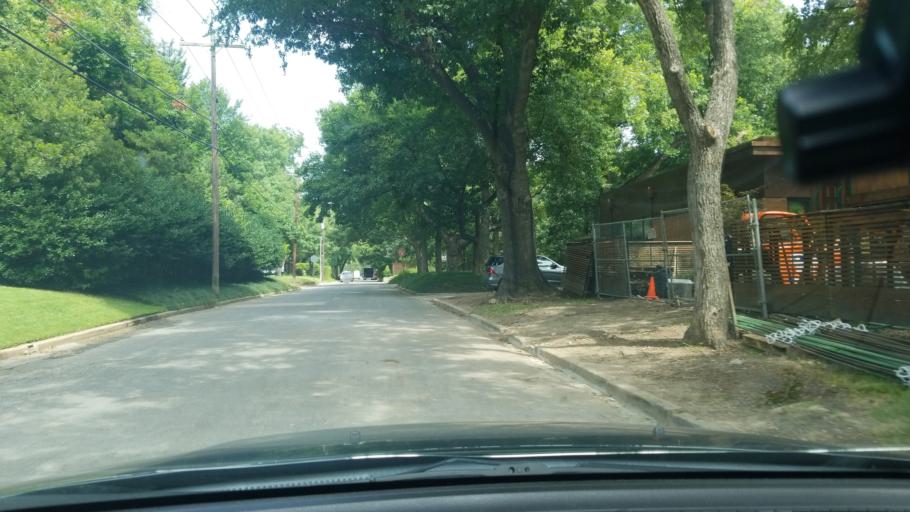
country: US
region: Texas
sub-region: Dallas County
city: Highland Park
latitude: 32.8103
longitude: -96.7162
